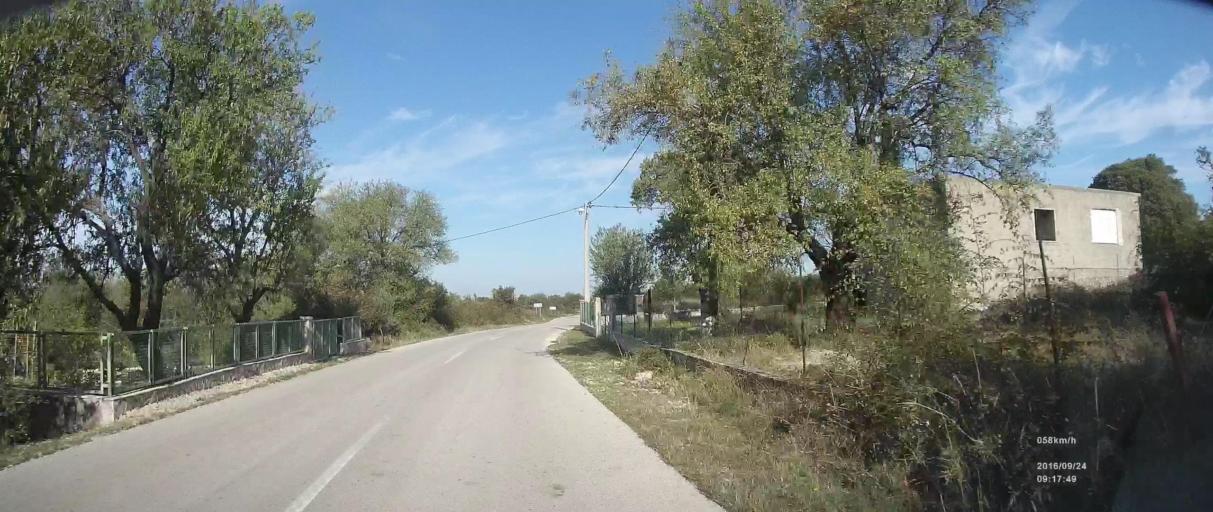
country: HR
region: Zadarska
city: Polaca
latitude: 44.0529
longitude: 15.5179
